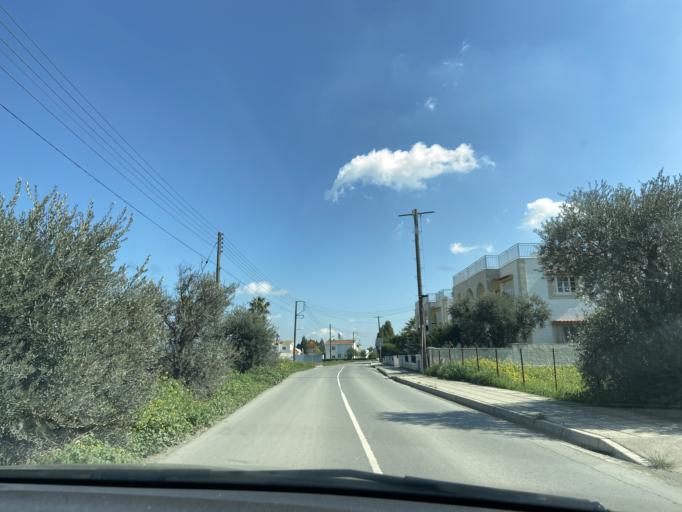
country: CY
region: Lefkosia
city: Dali
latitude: 35.0176
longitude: 33.3988
